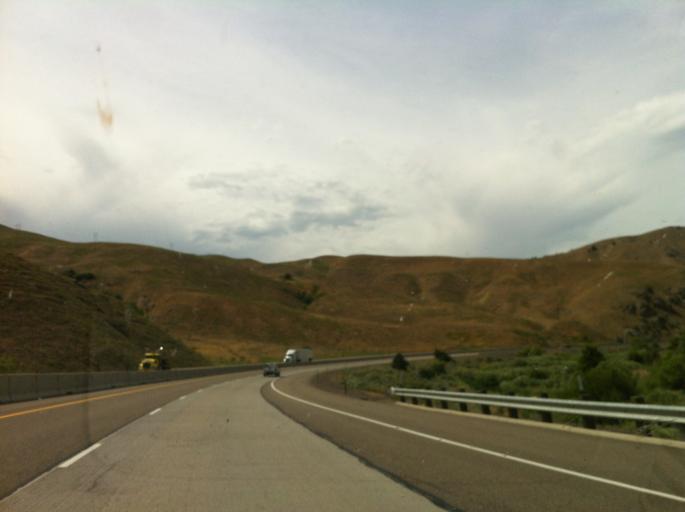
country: US
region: Idaho
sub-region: Washington County
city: Weiser
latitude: 44.3668
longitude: -117.2946
